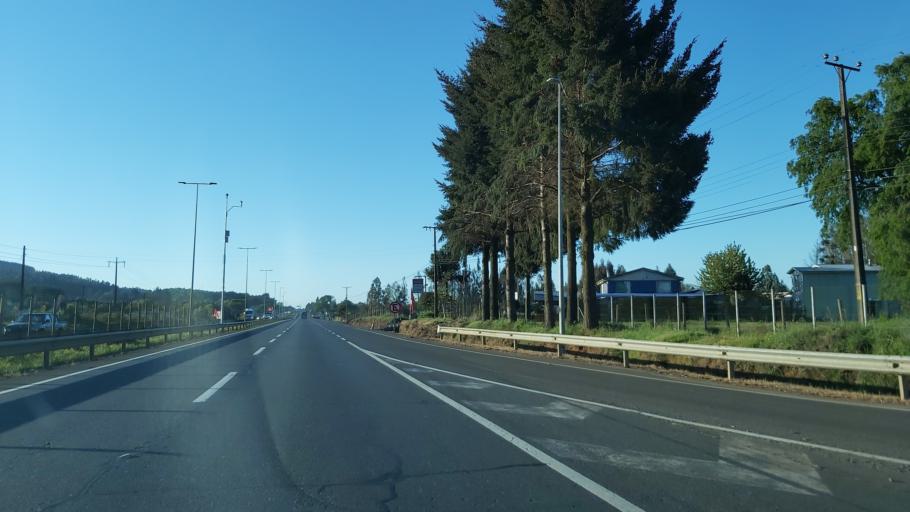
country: CL
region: Araucania
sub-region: Provincia de Malleco
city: Victoria
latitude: -38.1315
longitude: -72.3243
